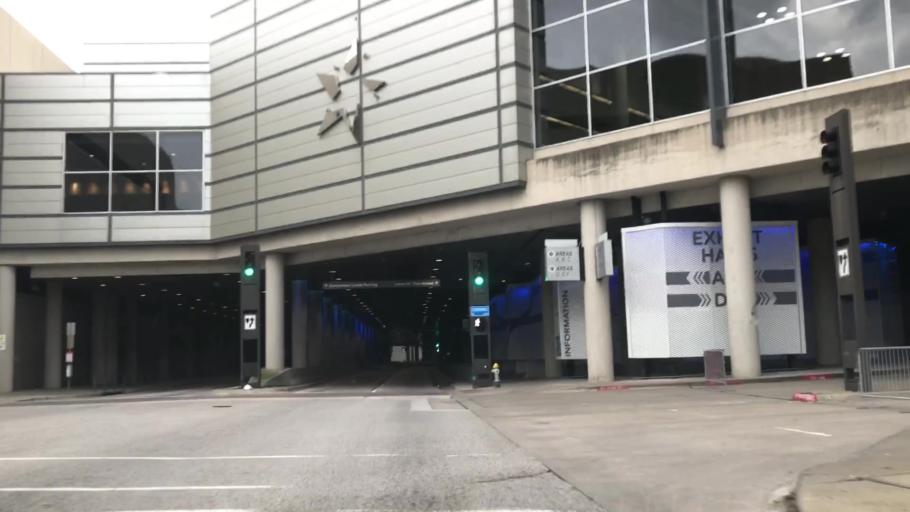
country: US
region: Texas
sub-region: Dallas County
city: Dallas
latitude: 32.7747
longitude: -96.8029
